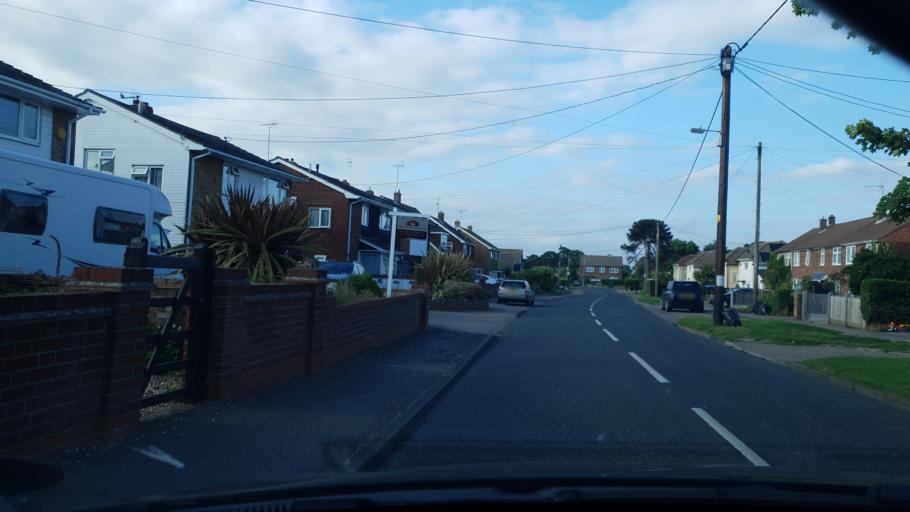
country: GB
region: England
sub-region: Essex
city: Frinton-on-Sea
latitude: 51.8509
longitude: 1.2249
